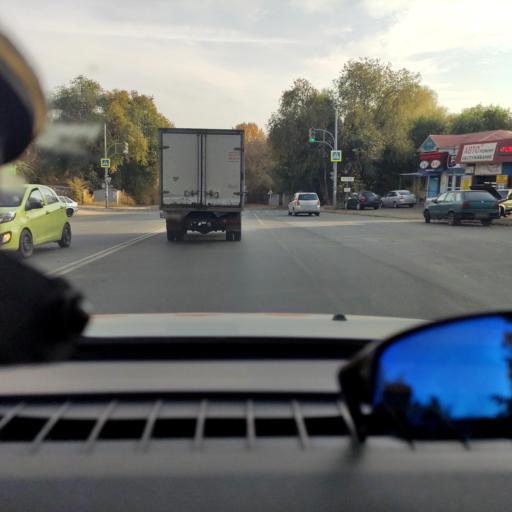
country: RU
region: Samara
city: Samara
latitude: 53.2423
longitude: 50.2558
